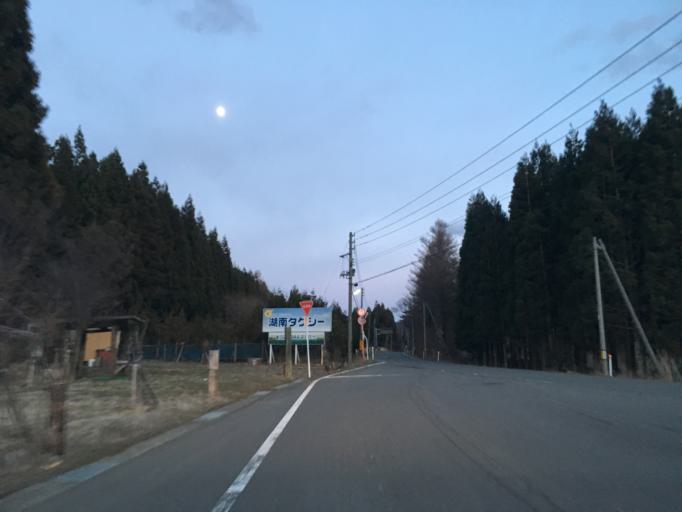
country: JP
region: Fukushima
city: Inawashiro
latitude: 37.4013
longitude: 140.1502
